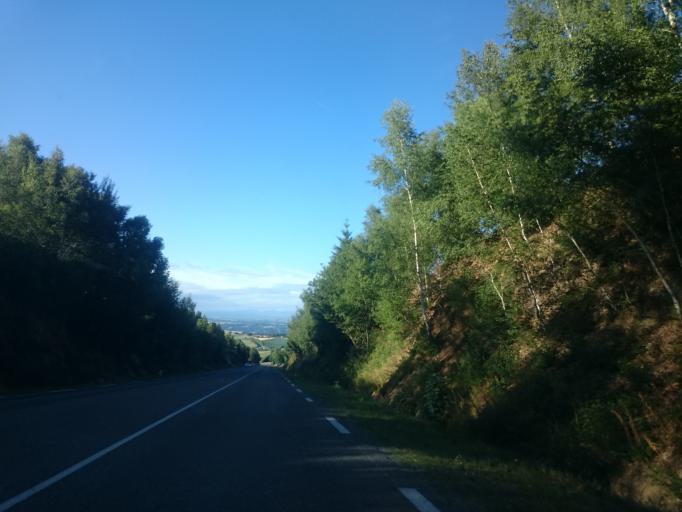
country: FR
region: Midi-Pyrenees
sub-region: Departement de l'Aveyron
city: Entraygues-sur-Truyere
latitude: 44.7153
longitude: 2.5019
